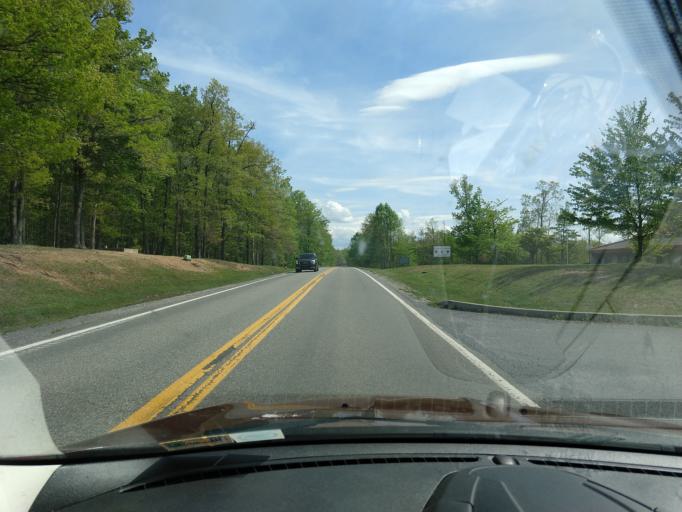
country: US
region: West Virginia
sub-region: Raleigh County
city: Stanaford
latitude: 37.7887
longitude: -81.1166
